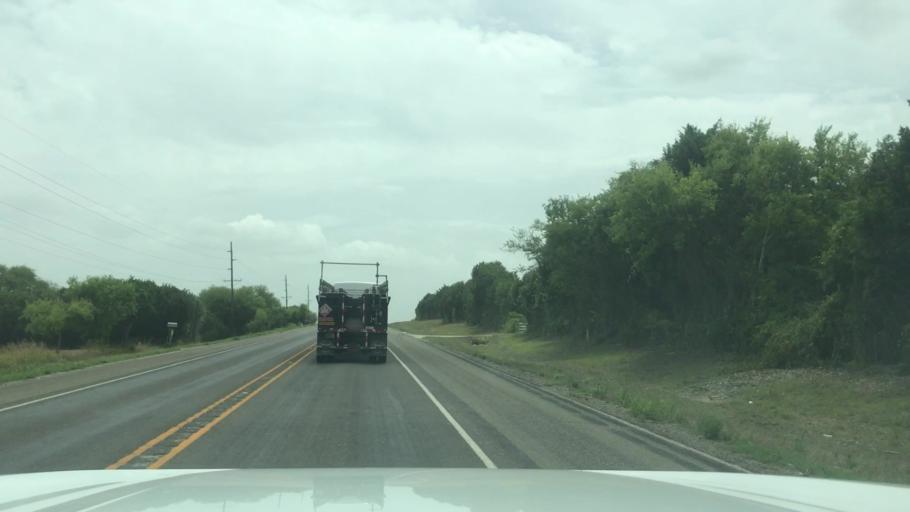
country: US
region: Texas
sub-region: Bosque County
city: Clifton
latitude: 31.7233
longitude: -97.5487
